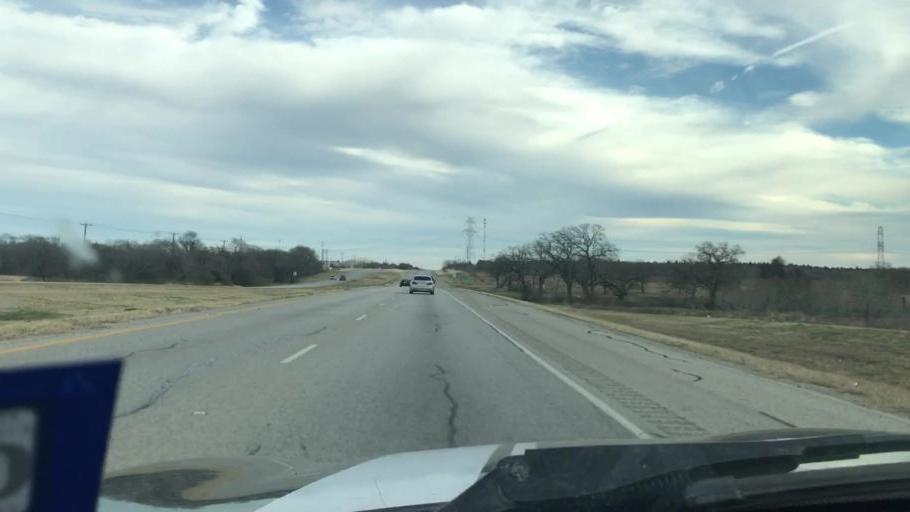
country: US
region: Texas
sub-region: Bastrop County
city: Elgin
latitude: 30.3323
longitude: -97.3530
